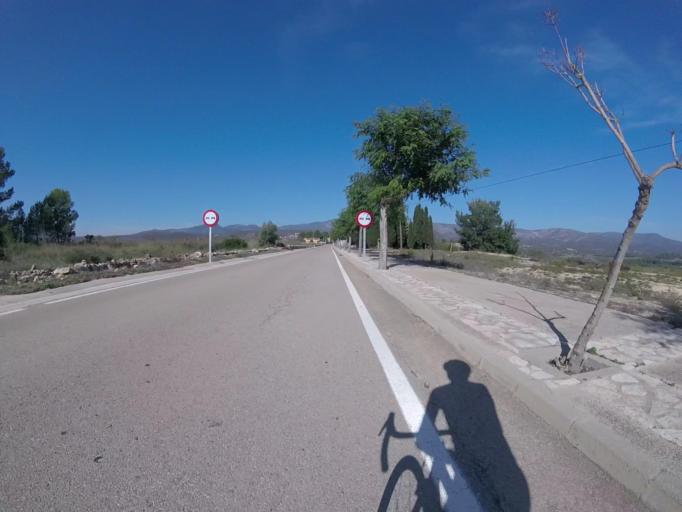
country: ES
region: Valencia
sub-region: Provincia de Castello
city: Cuevas de Vinroma
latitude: 40.2611
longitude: 0.0758
